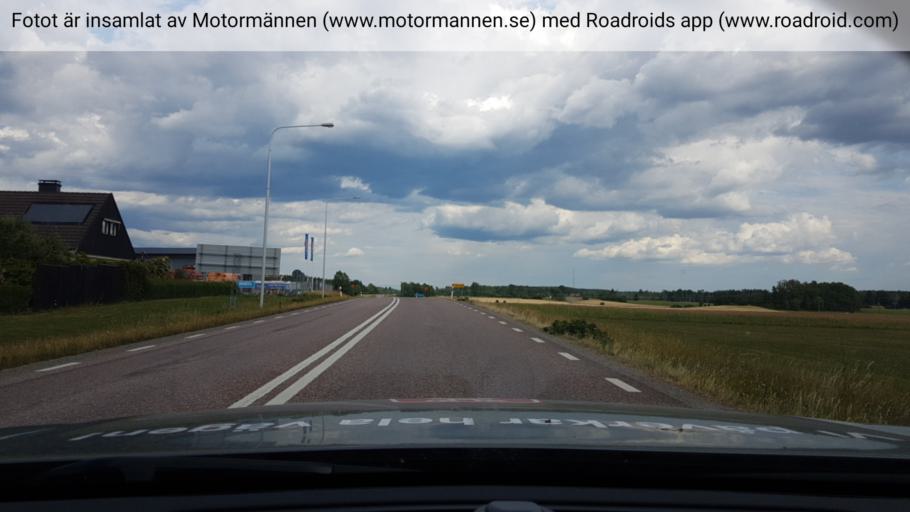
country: SE
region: Uppsala
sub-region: Heby Kommun
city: Heby
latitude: 59.9356
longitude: 16.8736
